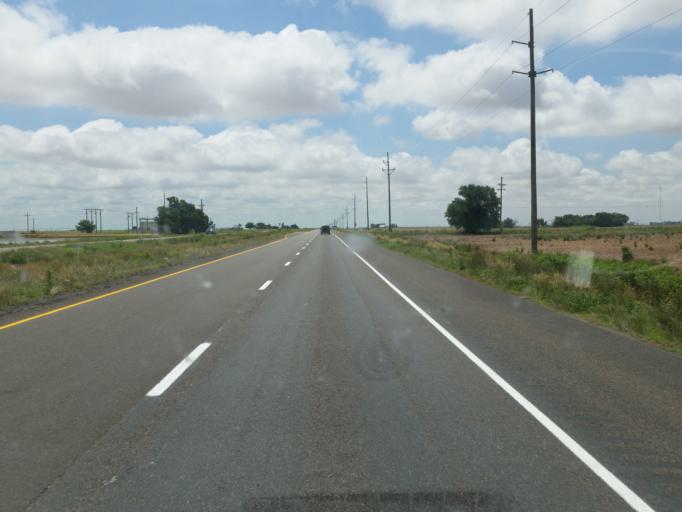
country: US
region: Texas
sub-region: Lubbock County
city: Slaton
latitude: 33.4051
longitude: -101.6199
